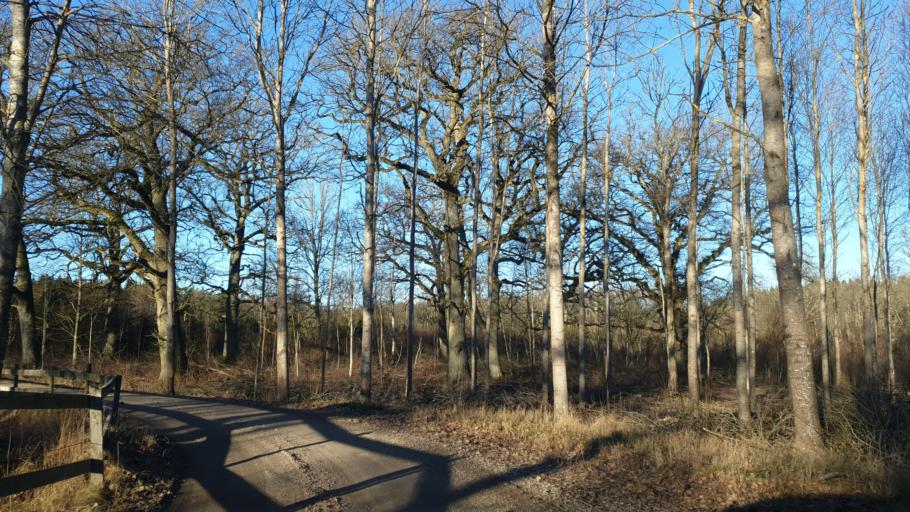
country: SE
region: Blekinge
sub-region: Karlskrona Kommun
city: Nattraby
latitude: 56.2589
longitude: 15.4182
